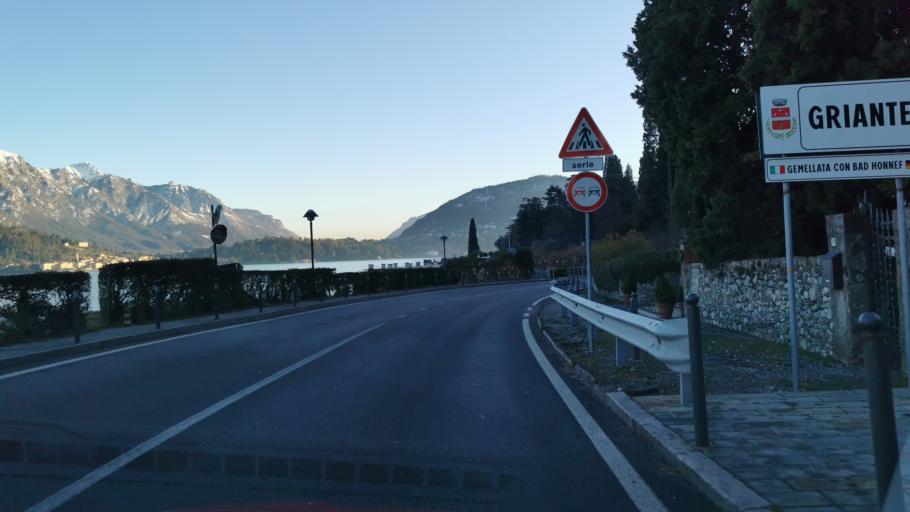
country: IT
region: Lombardy
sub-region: Provincia di Como
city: Griante
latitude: 46.0007
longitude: 9.2365
